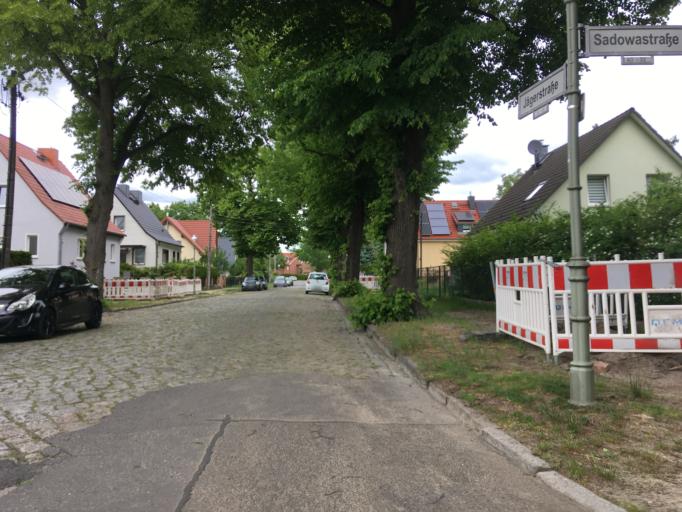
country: DE
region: Berlin
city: Kaulsdorf
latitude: 52.4820
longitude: 13.5823
